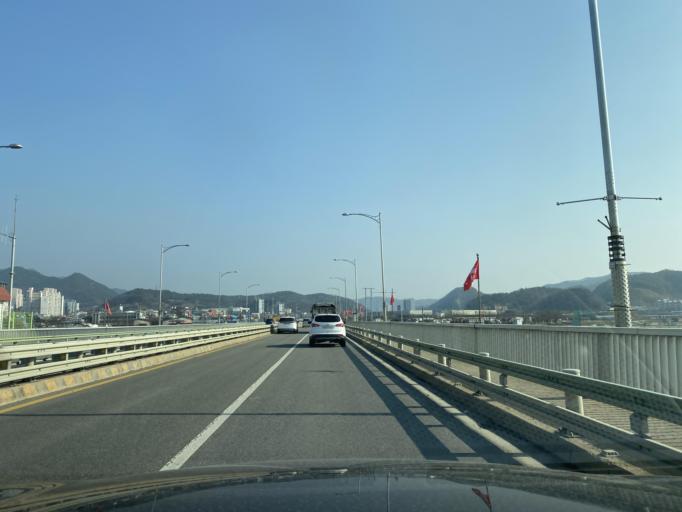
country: KR
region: Chungcheongnam-do
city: Yesan
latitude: 36.6841
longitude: 126.8206
